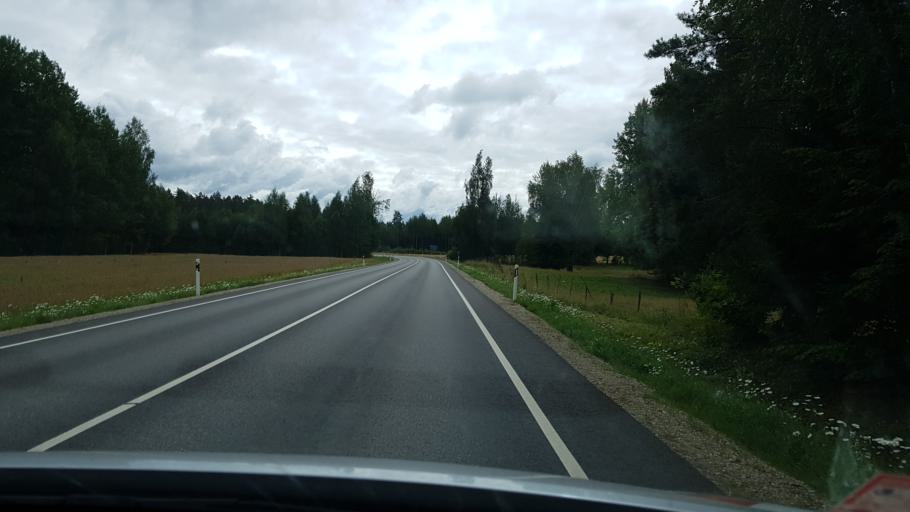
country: EE
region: Polvamaa
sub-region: Polva linn
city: Polva
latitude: 58.0051
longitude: 27.2067
